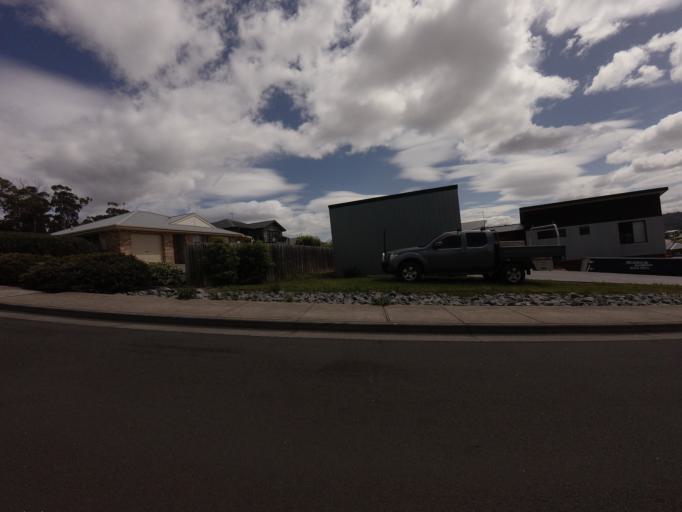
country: AU
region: Tasmania
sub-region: Clarence
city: Howrah
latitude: -42.8913
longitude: 147.4227
